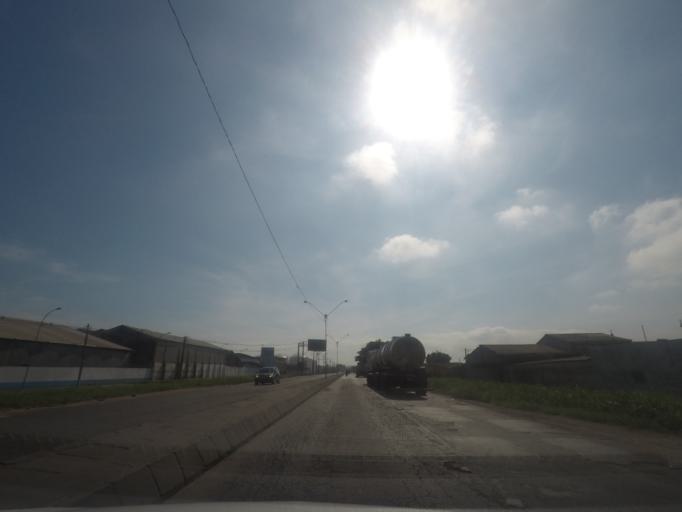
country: BR
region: Parana
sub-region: Paranagua
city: Paranagua
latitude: -25.5230
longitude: -48.5260
